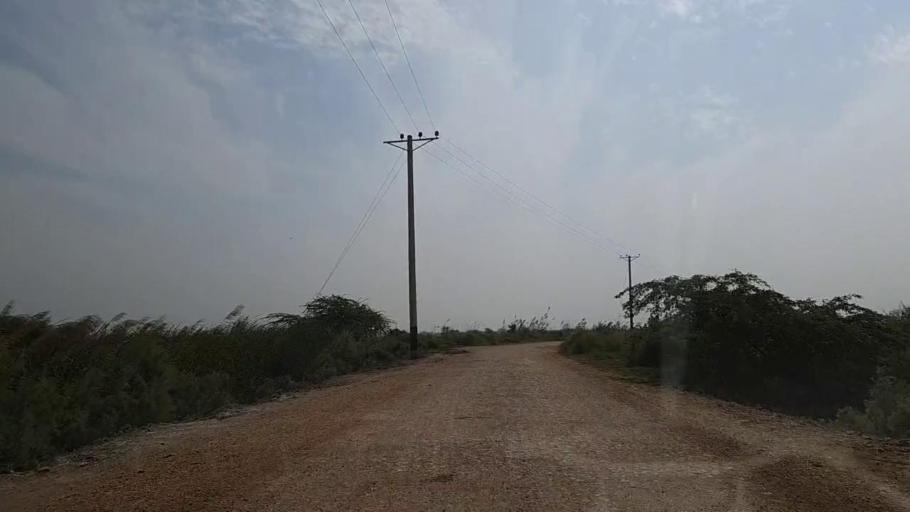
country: PK
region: Sindh
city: Mirpur Batoro
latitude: 24.6005
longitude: 68.2145
